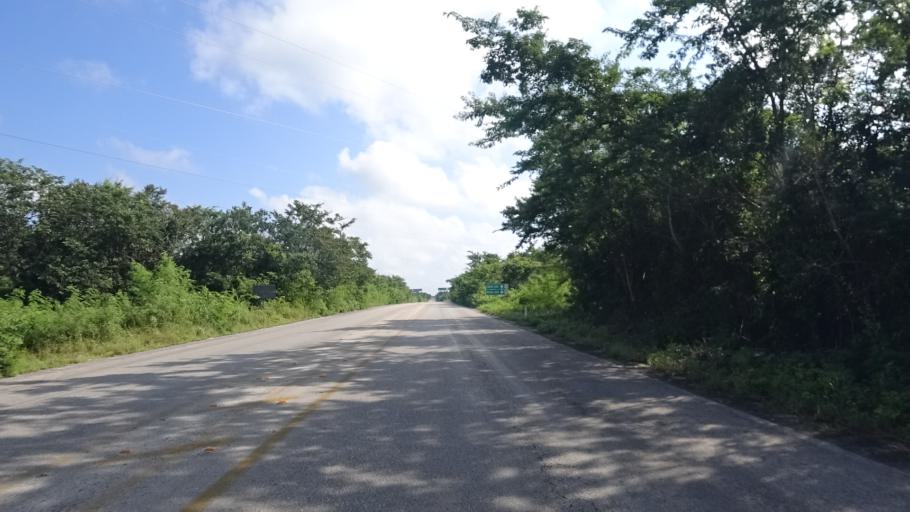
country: MX
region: Yucatan
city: Valladolid
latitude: 20.7005
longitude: -88.2427
